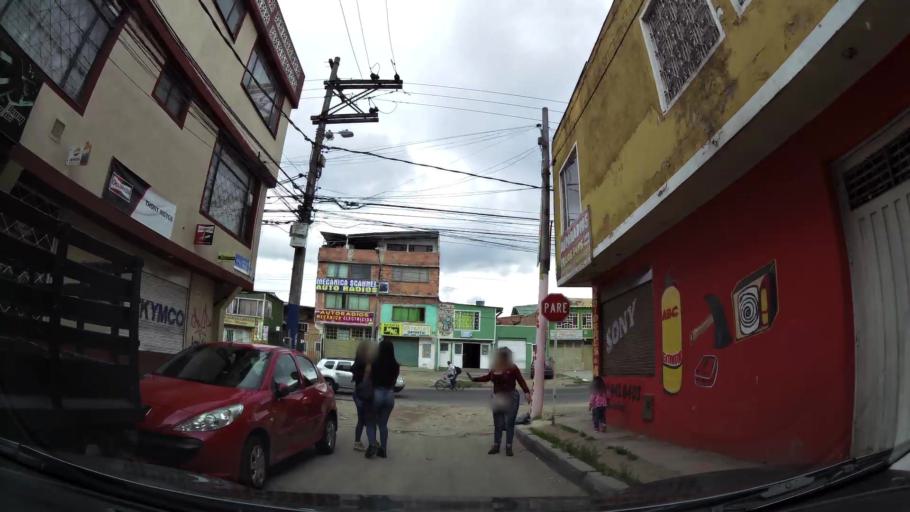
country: CO
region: Bogota D.C.
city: Barrio San Luis
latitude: 4.7145
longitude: -74.0966
